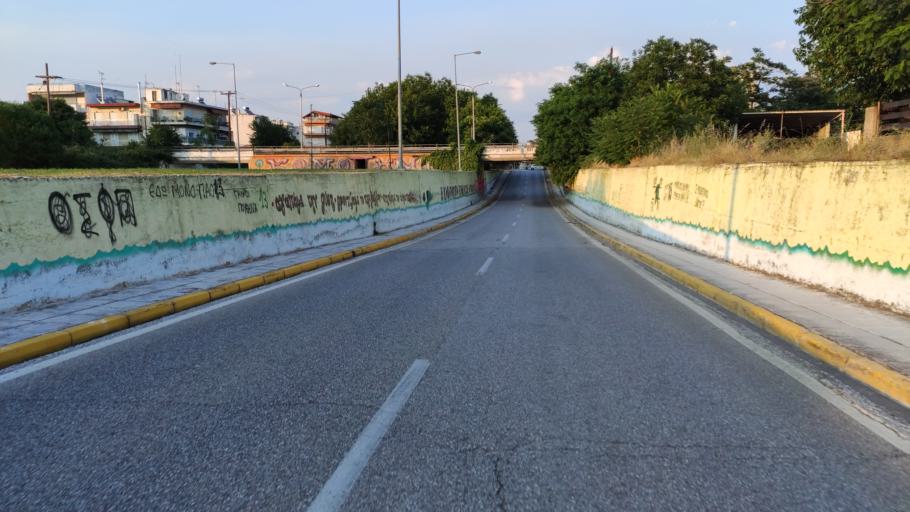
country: GR
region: East Macedonia and Thrace
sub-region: Nomos Rodopis
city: Komotini
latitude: 41.1142
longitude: 25.3903
